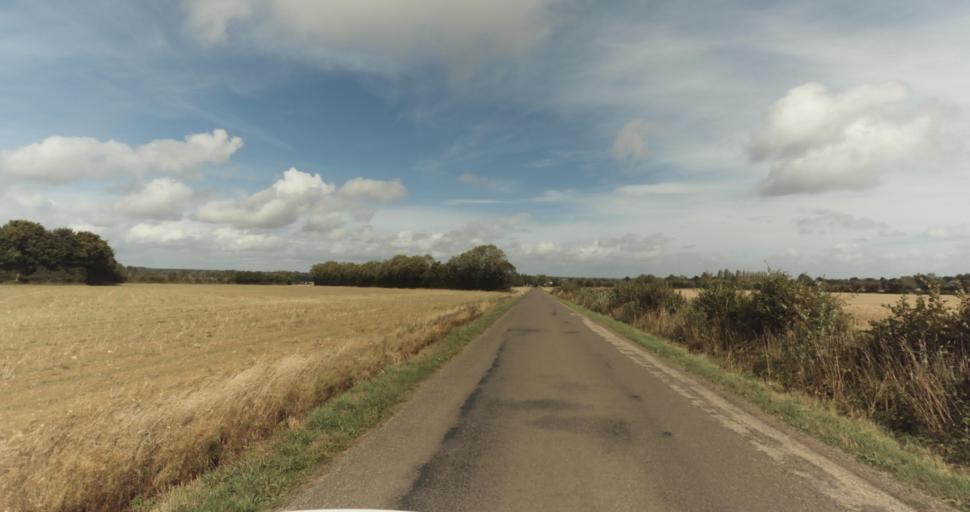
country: FR
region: Lower Normandy
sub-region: Departement de l'Orne
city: Gace
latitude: 48.8187
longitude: 0.3842
